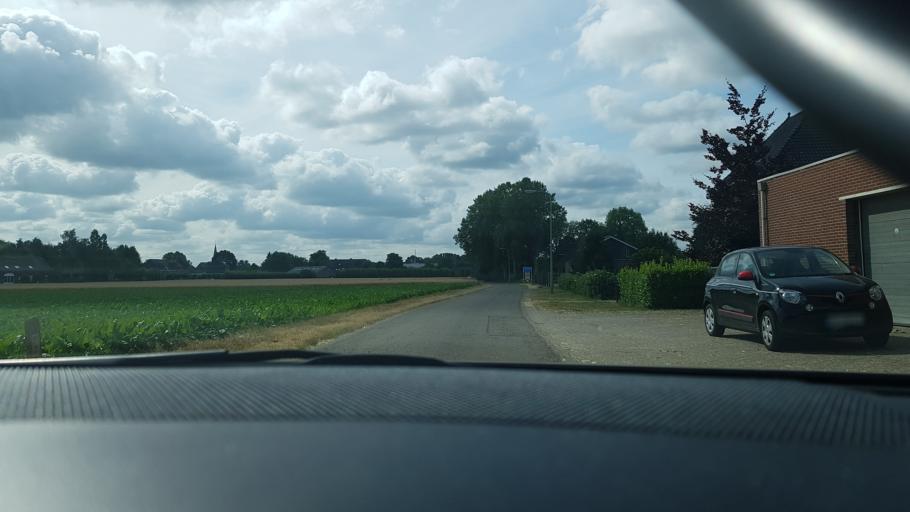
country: NL
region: Limburg
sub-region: Gemeente Beesel
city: Beesel
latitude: 51.2381
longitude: 6.0252
